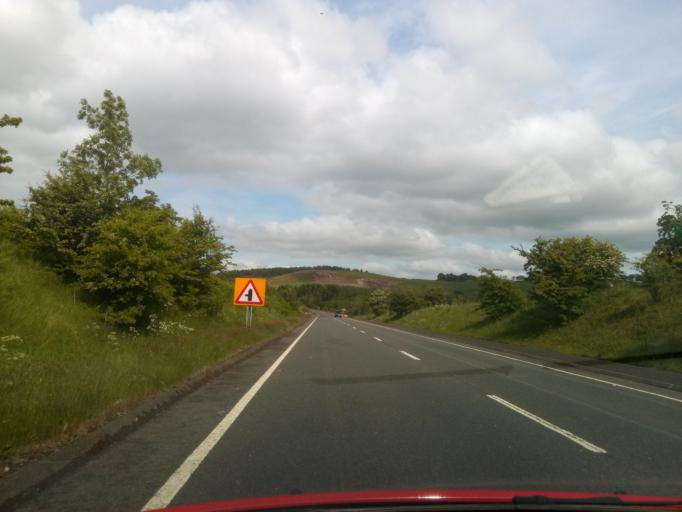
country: GB
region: Scotland
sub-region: The Scottish Borders
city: Selkirk
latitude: 55.5316
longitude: -2.8268
